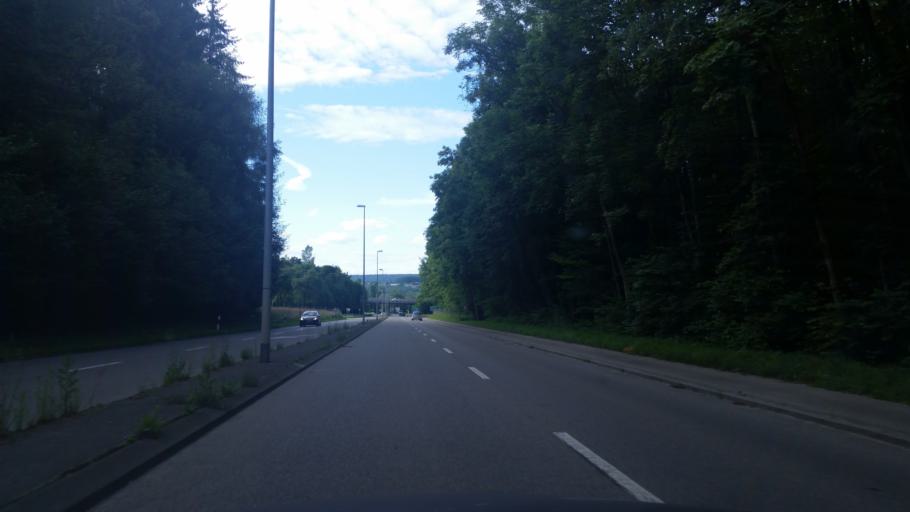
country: CH
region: Thurgau
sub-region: Frauenfeld District
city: Gachnang
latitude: 47.5577
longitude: 8.8704
